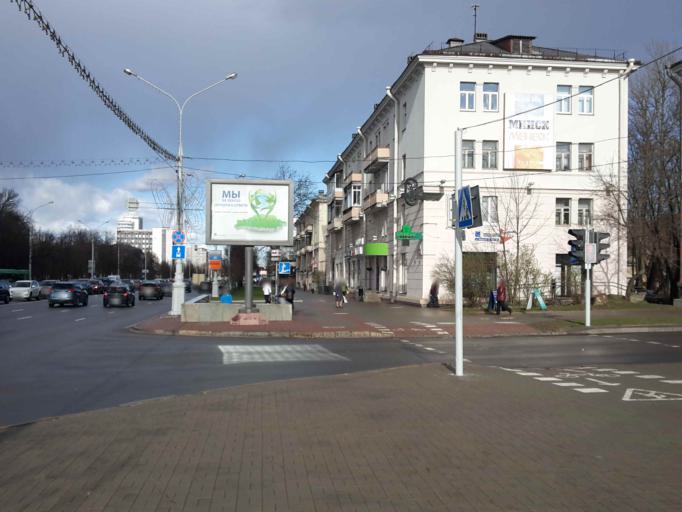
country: BY
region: Minsk
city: Minsk
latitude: 53.9274
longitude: 27.6263
